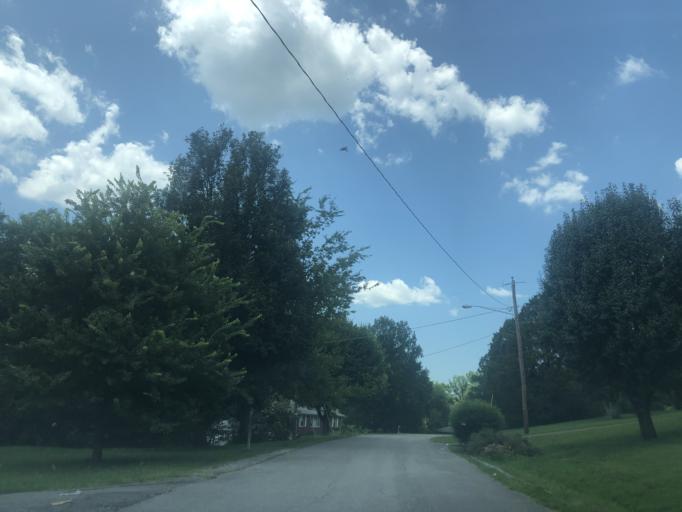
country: US
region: Tennessee
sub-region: Davidson County
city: Nashville
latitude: 36.1753
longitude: -86.6964
